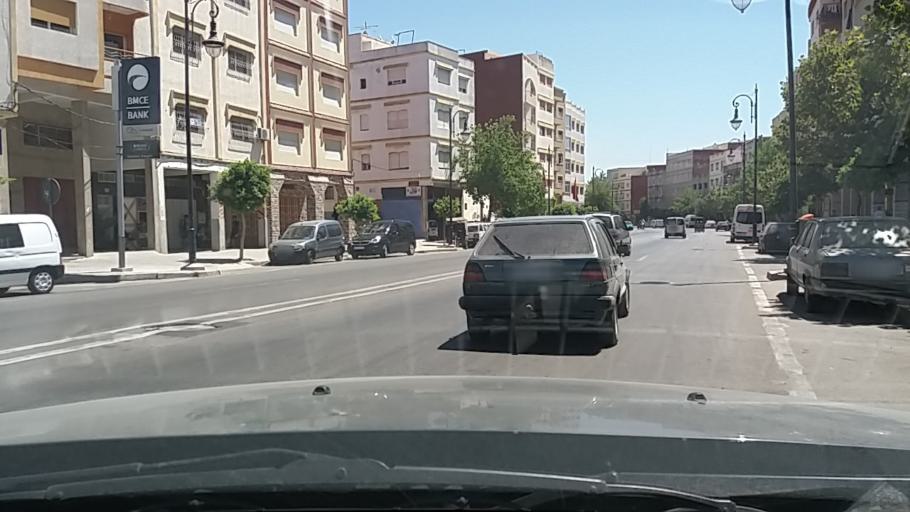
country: MA
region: Tanger-Tetouan
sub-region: Tanger-Assilah
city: Tangier
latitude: 35.7520
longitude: -5.8043
